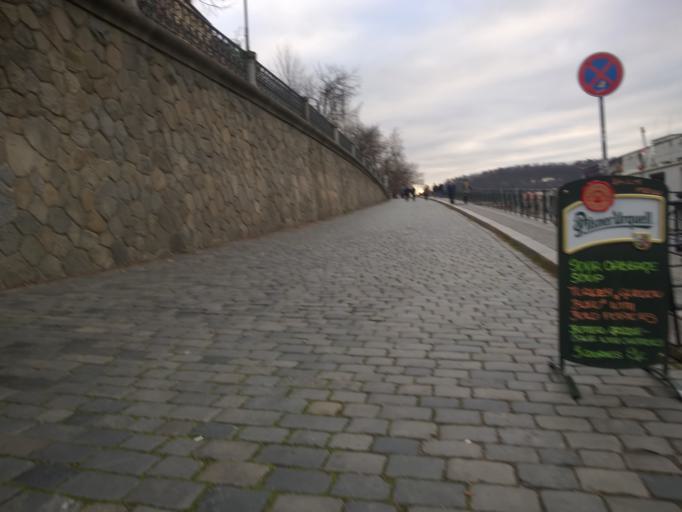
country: CZ
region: Praha
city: Prague
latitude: 50.0914
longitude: 14.4158
